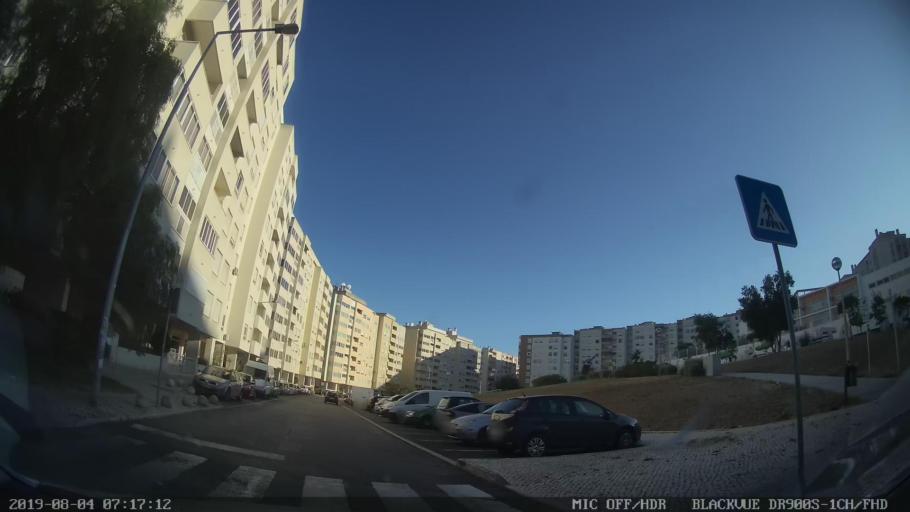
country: PT
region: Lisbon
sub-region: Vila Franca de Xira
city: Vialonga
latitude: 38.8682
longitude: -9.0655
